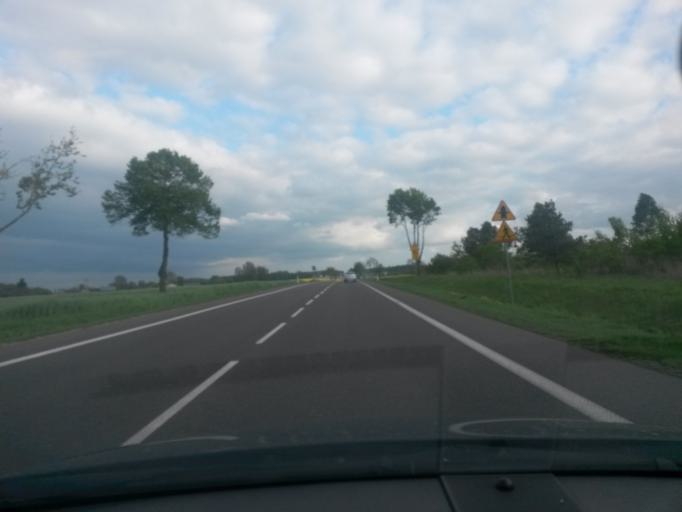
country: PL
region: Masovian Voivodeship
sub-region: Powiat plocki
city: Drobin
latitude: 52.6852
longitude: 20.0557
